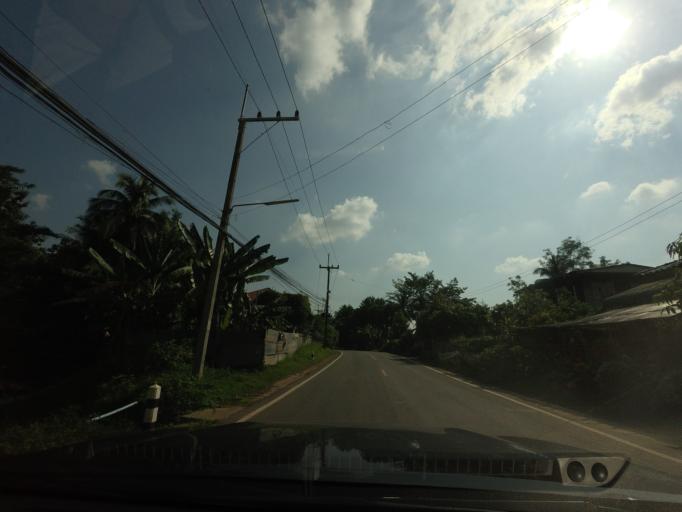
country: TH
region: Nan
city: Santi Suk
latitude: 18.9534
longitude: 100.9223
